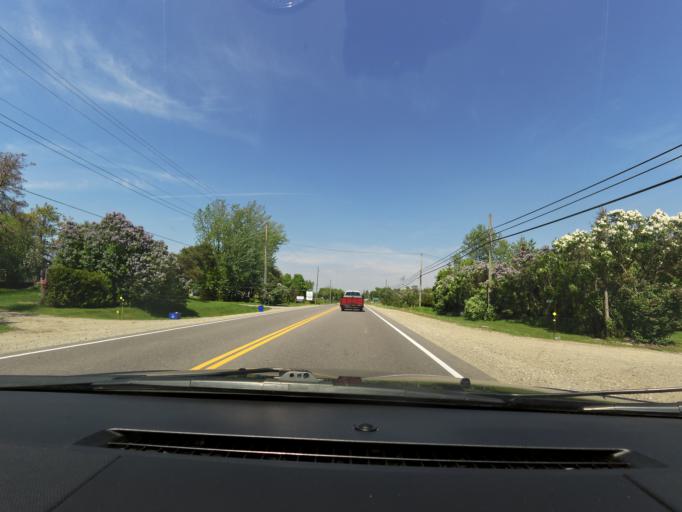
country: CA
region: Ontario
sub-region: Wellington County
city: Guelph
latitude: 43.6000
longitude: -80.1687
